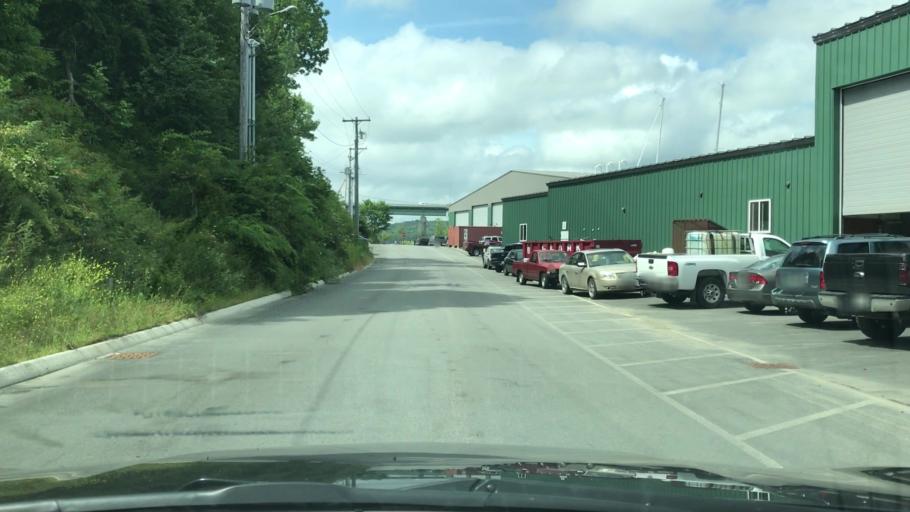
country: US
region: Maine
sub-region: Waldo County
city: Belfast
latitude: 44.4295
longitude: -69.0095
